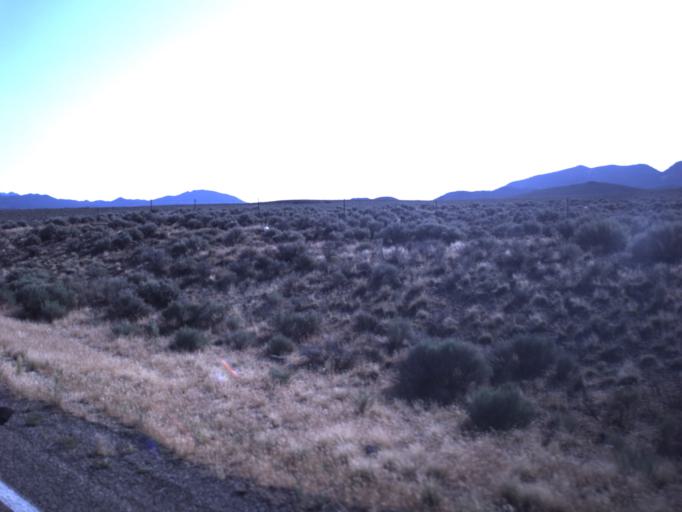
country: US
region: Utah
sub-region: Beaver County
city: Milford
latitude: 38.1583
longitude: -112.9571
